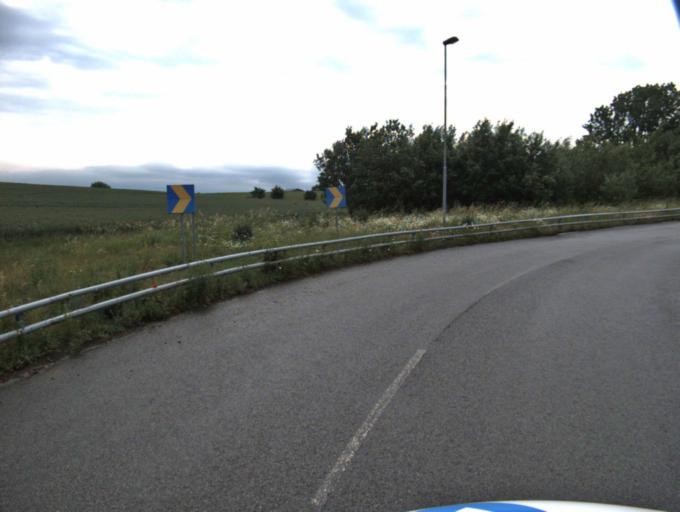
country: SE
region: Skane
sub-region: Kavlinge Kommun
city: Kaevlinge
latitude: 55.7694
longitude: 13.0881
